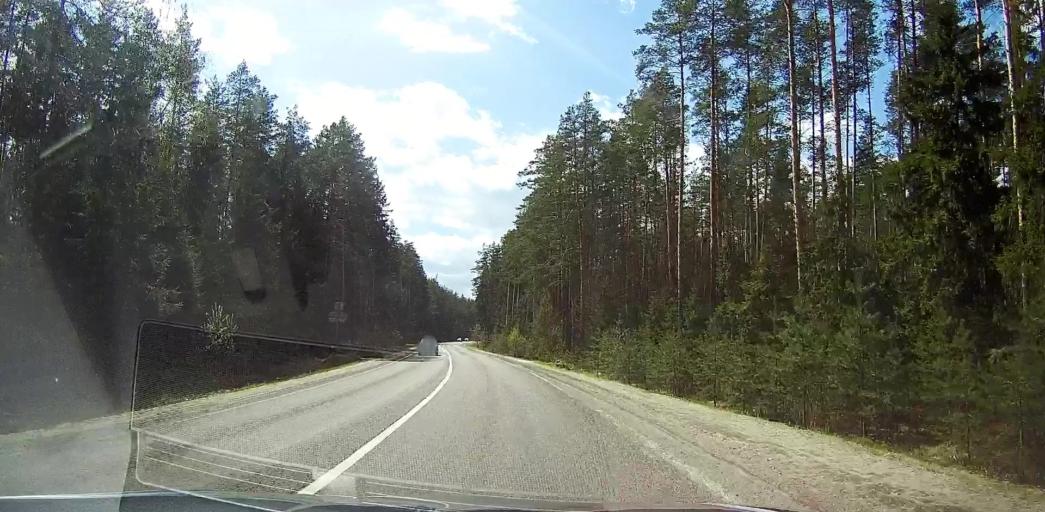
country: RU
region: Moskovskaya
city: Davydovo
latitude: 55.5614
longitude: 38.8473
